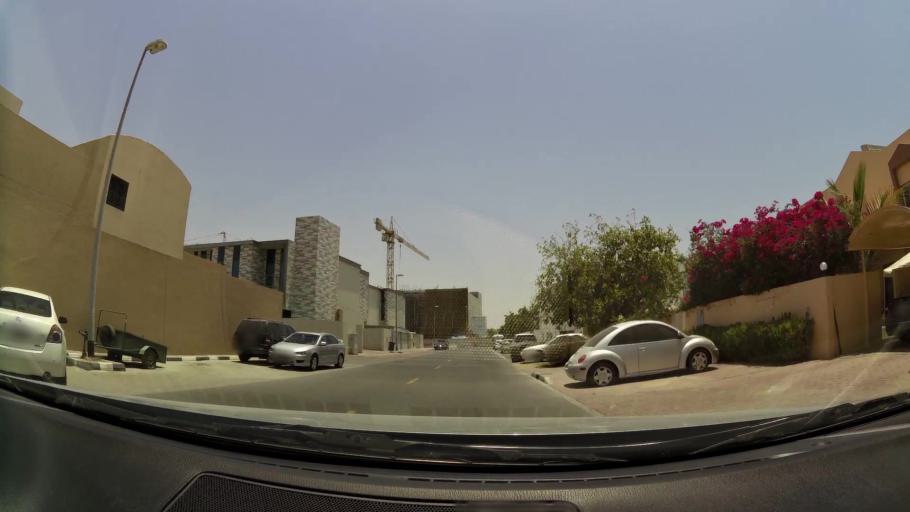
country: AE
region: Dubai
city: Dubai
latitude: 25.2217
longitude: 55.2611
